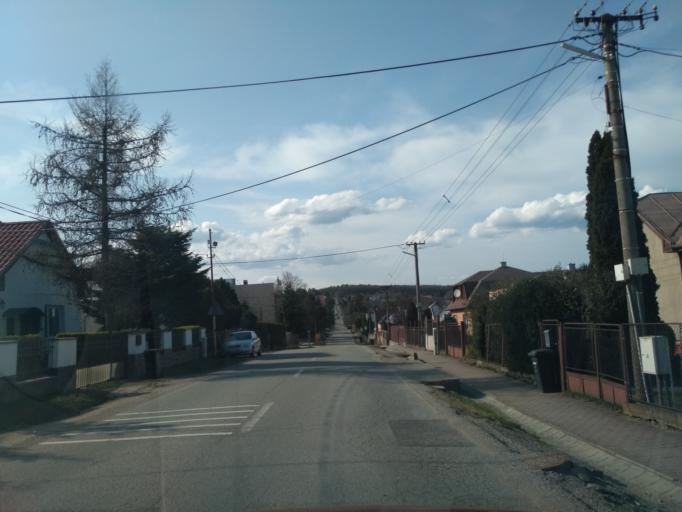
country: SK
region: Kosicky
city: Kosice
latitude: 48.6881
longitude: 21.2130
